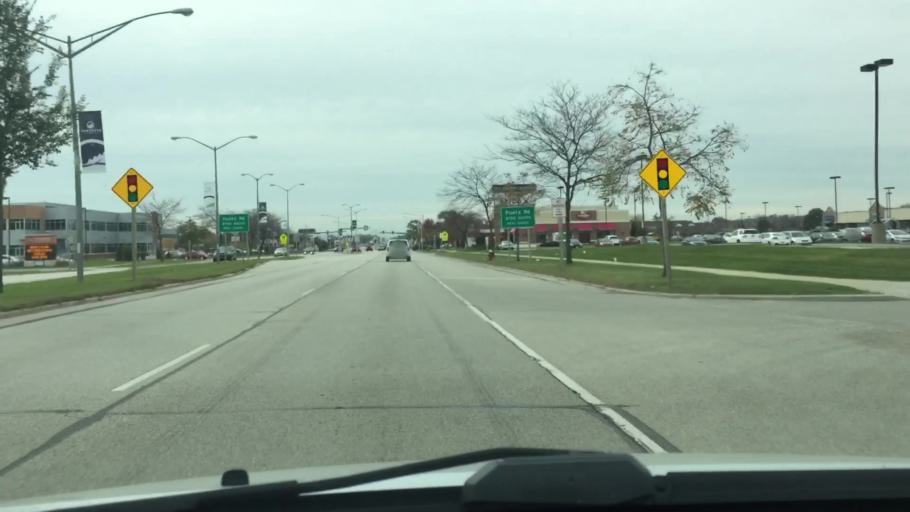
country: US
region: Wisconsin
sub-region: Milwaukee County
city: Oak Creek
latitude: 42.8896
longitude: -87.9122
